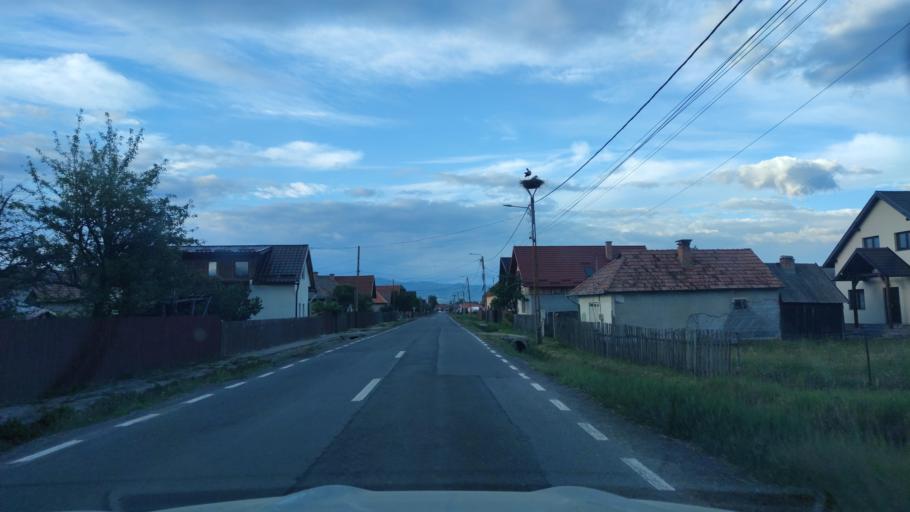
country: RO
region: Harghita
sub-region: Comuna Joseni
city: Joseni
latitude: 46.6996
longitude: 25.4860
